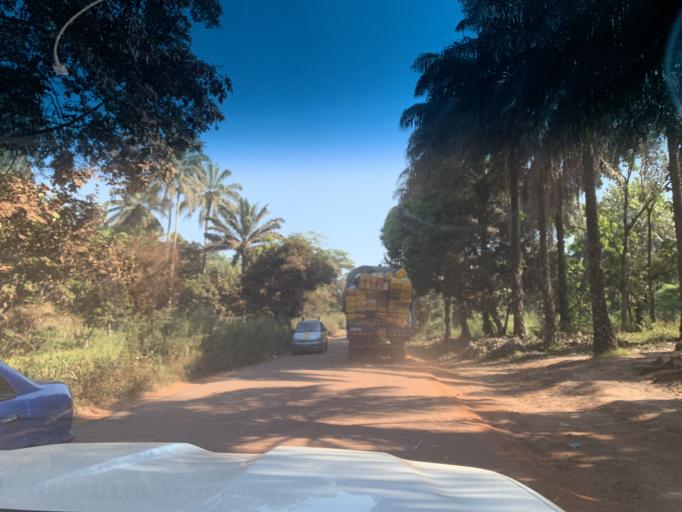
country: GN
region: Kindia
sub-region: Kindia
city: Kindia
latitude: 9.9405
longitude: -12.9735
